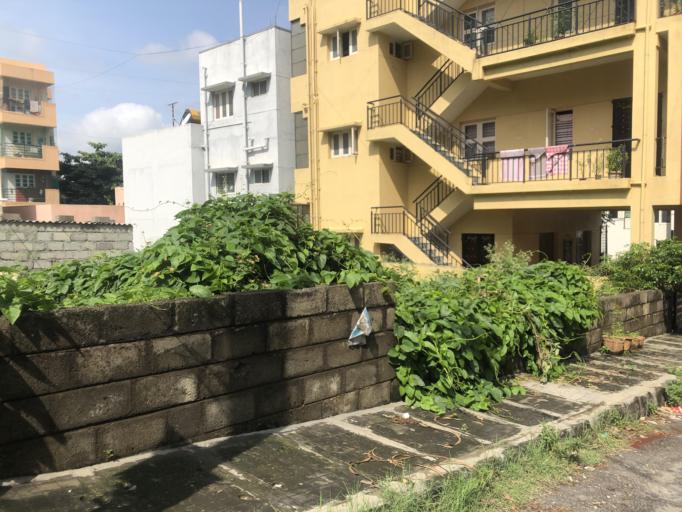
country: IN
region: Karnataka
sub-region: Bangalore Urban
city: Bangalore
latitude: 12.9212
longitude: 77.5277
